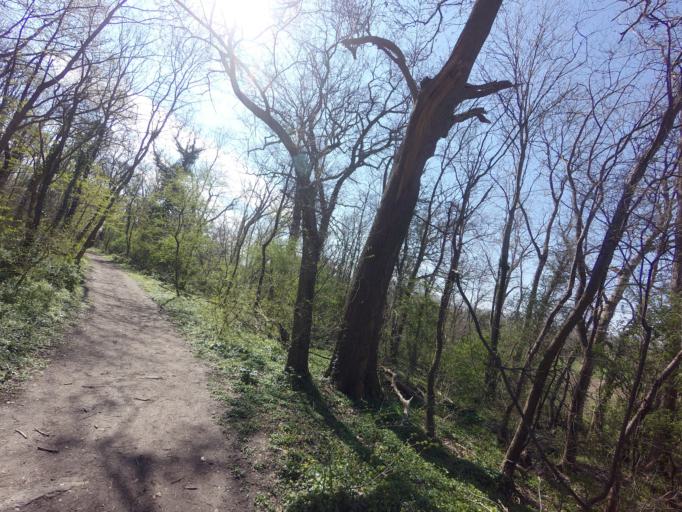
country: NL
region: Limburg
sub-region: Gemeente Maastricht
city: Maastricht
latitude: 50.8186
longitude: 5.6634
